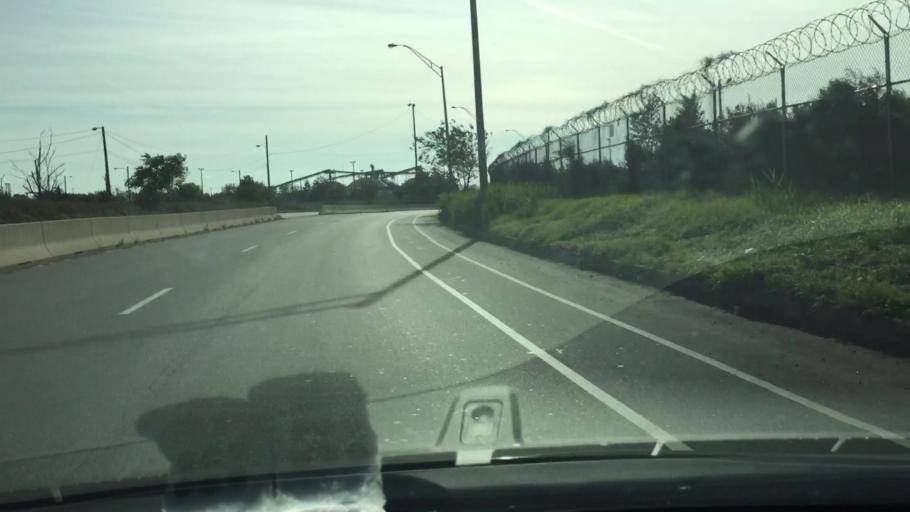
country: US
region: New Jersey
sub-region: Camden County
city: Gloucester City
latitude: 39.9040
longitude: -75.1404
